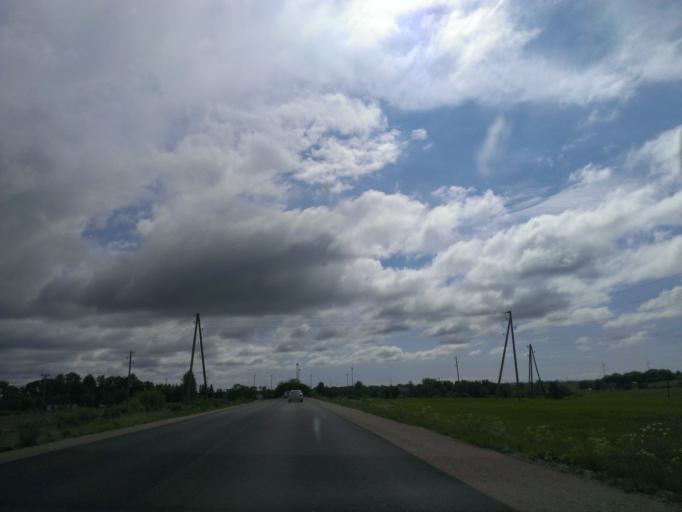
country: LV
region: Durbe
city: Liegi
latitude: 56.5599
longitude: 21.2630
